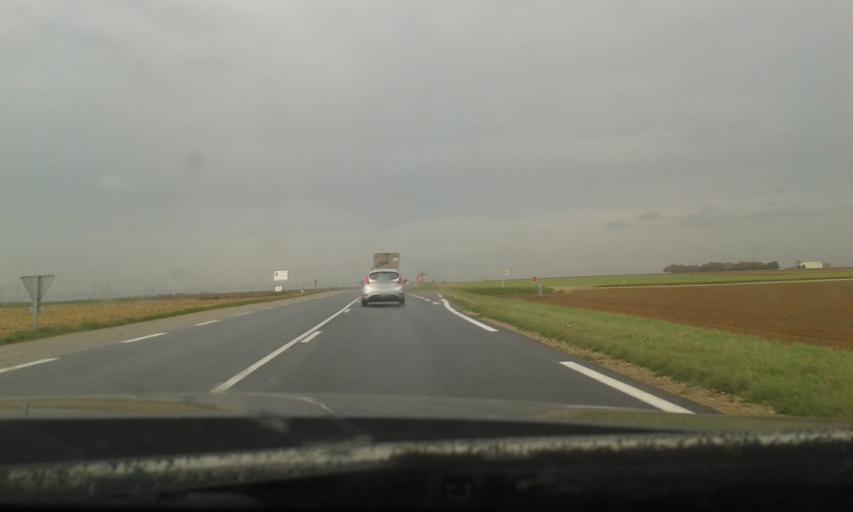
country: FR
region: Centre
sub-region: Departement d'Eure-et-Loir
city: Janville
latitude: 48.2373
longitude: 1.7843
